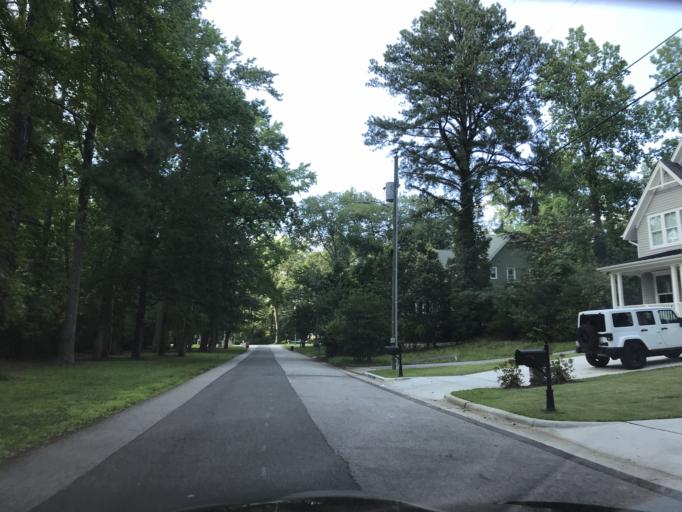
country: US
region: North Carolina
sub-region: Wake County
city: West Raleigh
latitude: 35.8072
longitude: -78.6736
